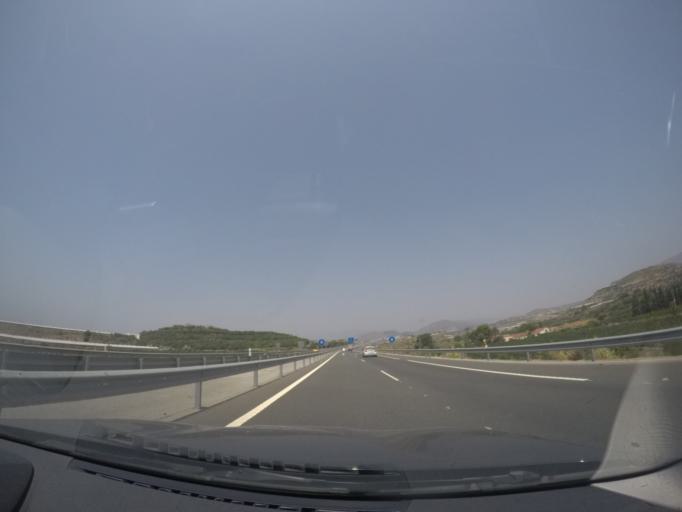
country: ES
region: Andalusia
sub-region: Provincia de Granada
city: Motril
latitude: 36.7342
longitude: -3.4801
